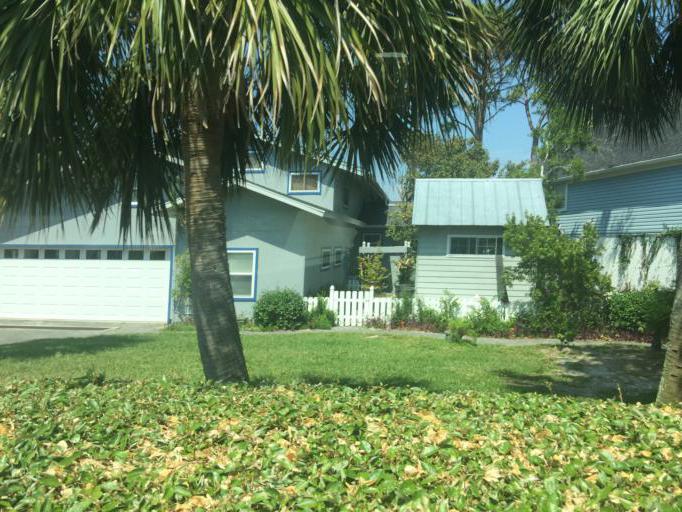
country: US
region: Florida
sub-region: Bay County
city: Lower Grand Lagoon
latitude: 30.1599
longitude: -85.7723
